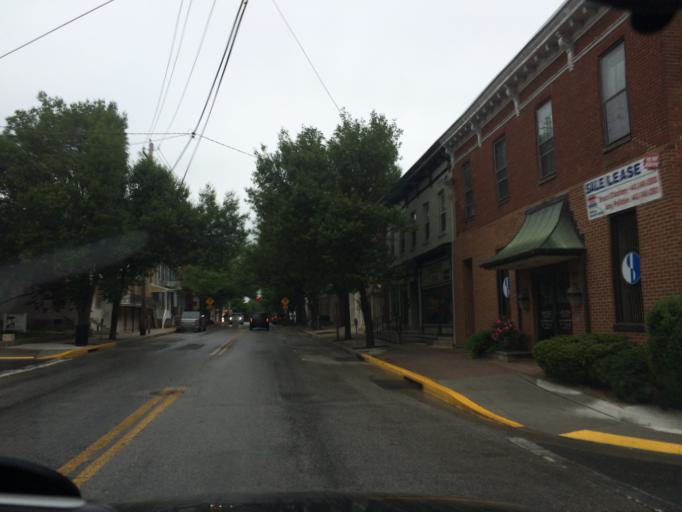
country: US
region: Maryland
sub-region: Carroll County
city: Westminster
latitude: 39.5698
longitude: -76.9905
